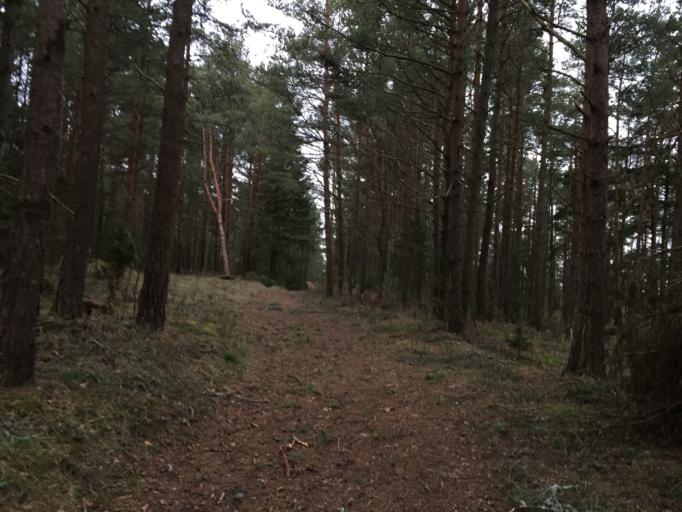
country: EE
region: Saare
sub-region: Kuressaare linn
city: Kuressaare
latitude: 58.5679
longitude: 22.2862
